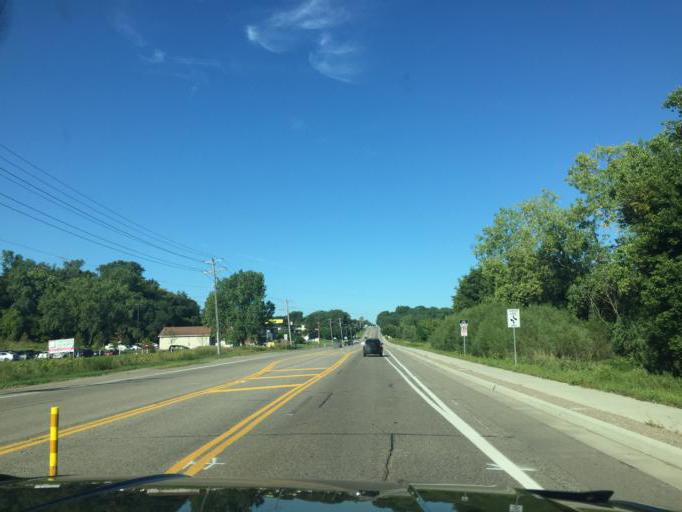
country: US
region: Minnesota
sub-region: Ramsey County
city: Little Canada
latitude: 44.9919
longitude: -93.1117
